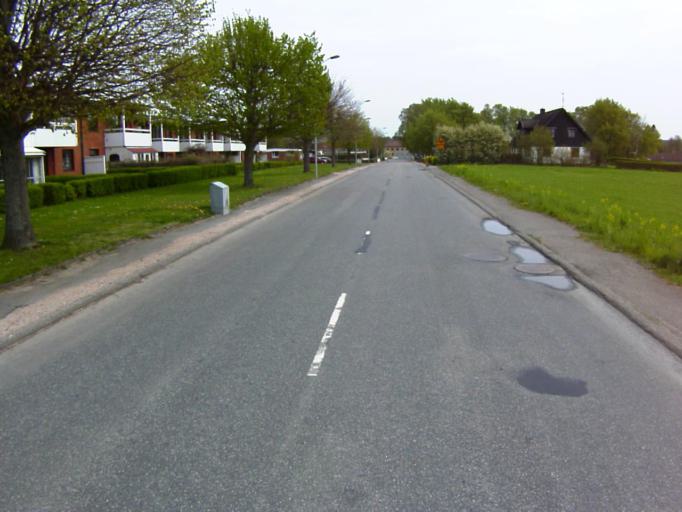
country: SE
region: Skane
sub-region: Kristianstads Kommun
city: Onnestad
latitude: 55.9336
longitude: 13.9612
